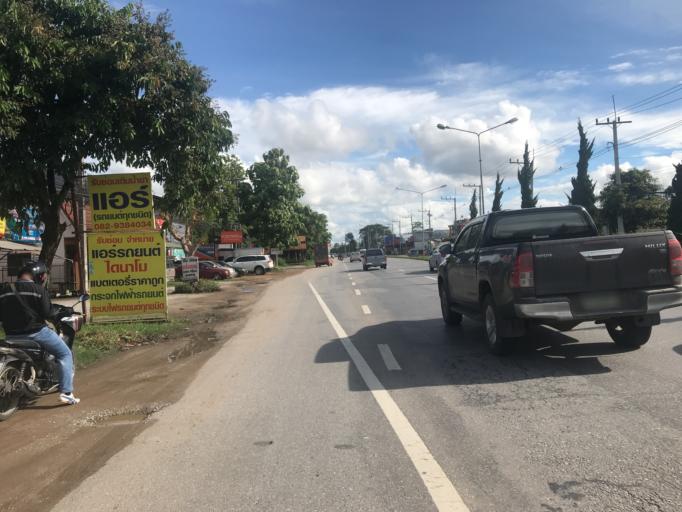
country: TH
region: Chiang Rai
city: Chiang Rai
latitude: 19.9519
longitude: 99.8496
